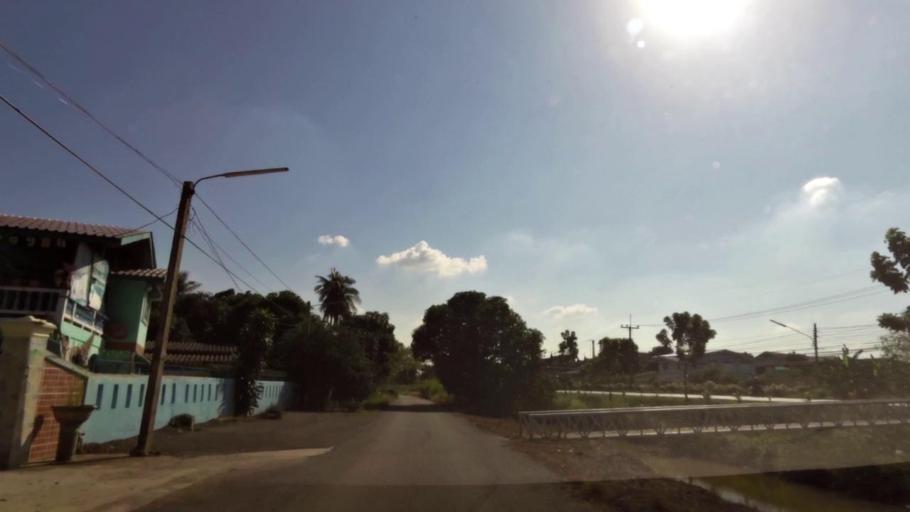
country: TH
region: Ang Thong
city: Ang Thong
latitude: 14.5916
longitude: 100.4697
